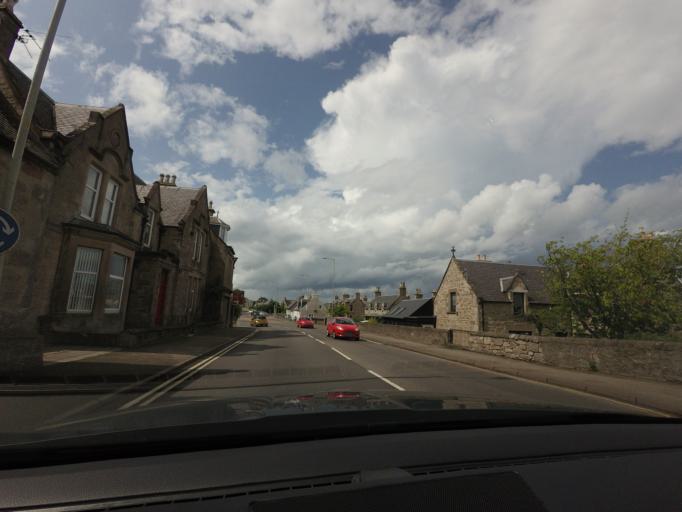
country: GB
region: Scotland
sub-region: Highland
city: Nairn
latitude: 57.5865
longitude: -3.8673
